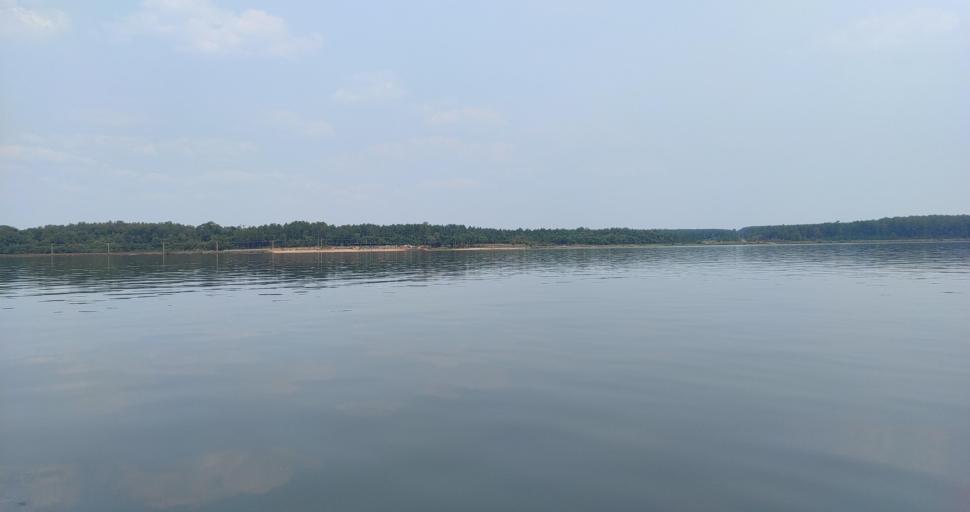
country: AR
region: Misiones
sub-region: Departamento de Candelaria
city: Candelaria
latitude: -27.4454
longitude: -55.7846
